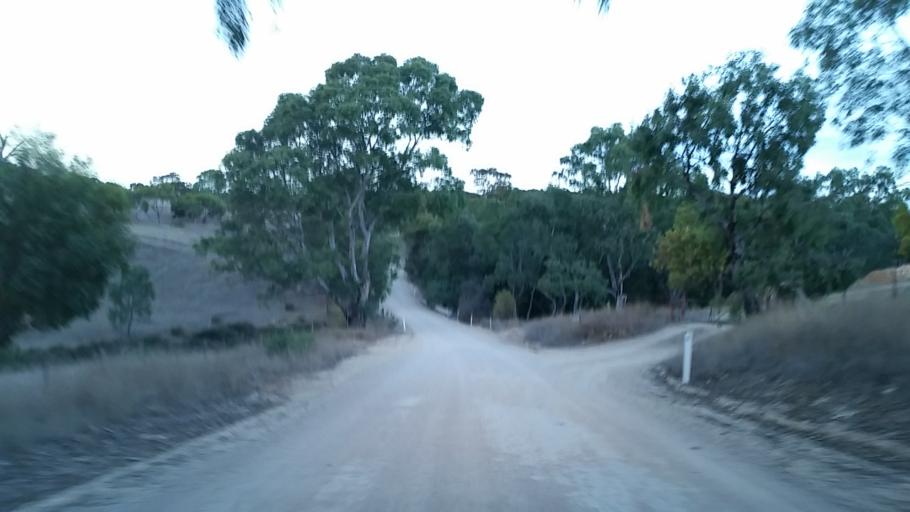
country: AU
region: South Australia
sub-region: Mount Barker
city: Nairne
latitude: -35.0930
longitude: 138.9559
